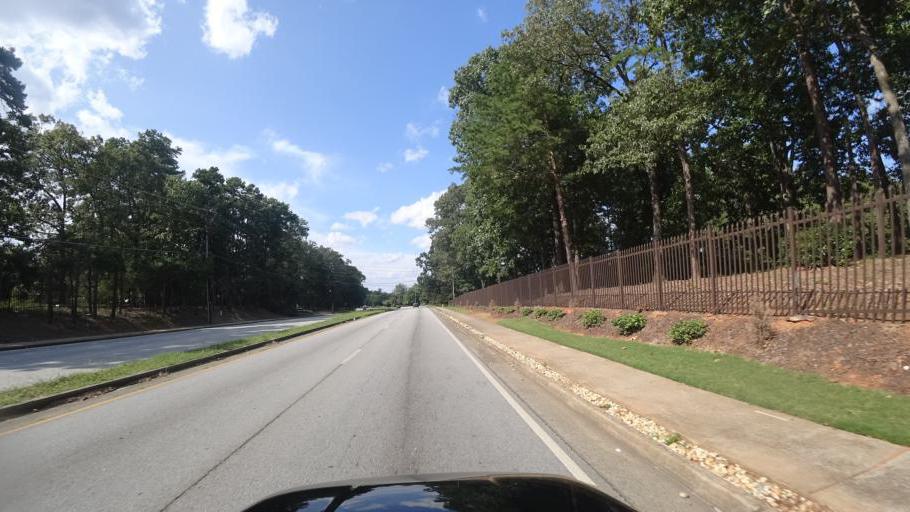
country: US
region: Georgia
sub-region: DeKalb County
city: Stone Mountain
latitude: 33.8180
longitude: -84.1935
